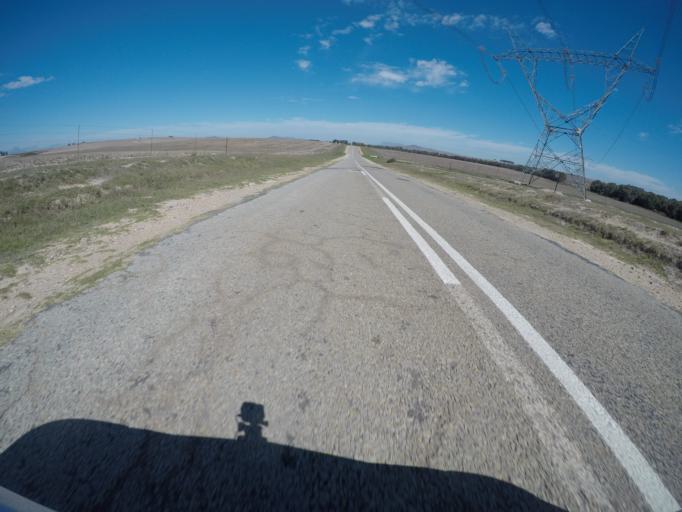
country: ZA
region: Western Cape
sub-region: City of Cape Town
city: Atlantis
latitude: -33.5992
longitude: 18.6422
